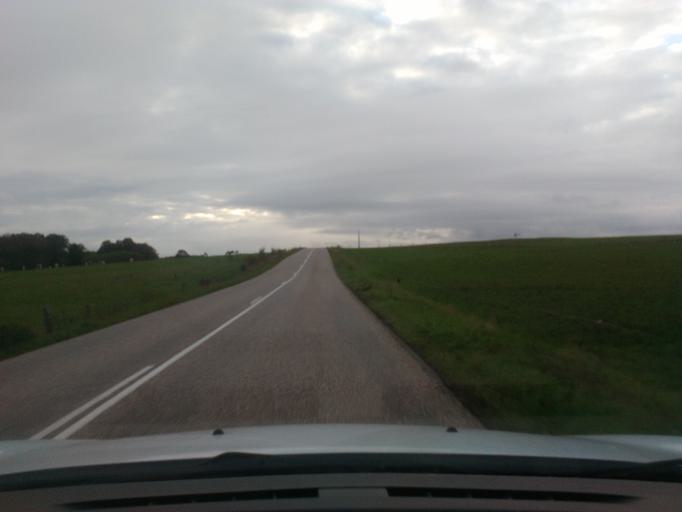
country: FR
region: Lorraine
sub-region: Departement des Vosges
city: Rambervillers
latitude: 48.3505
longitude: 6.5150
